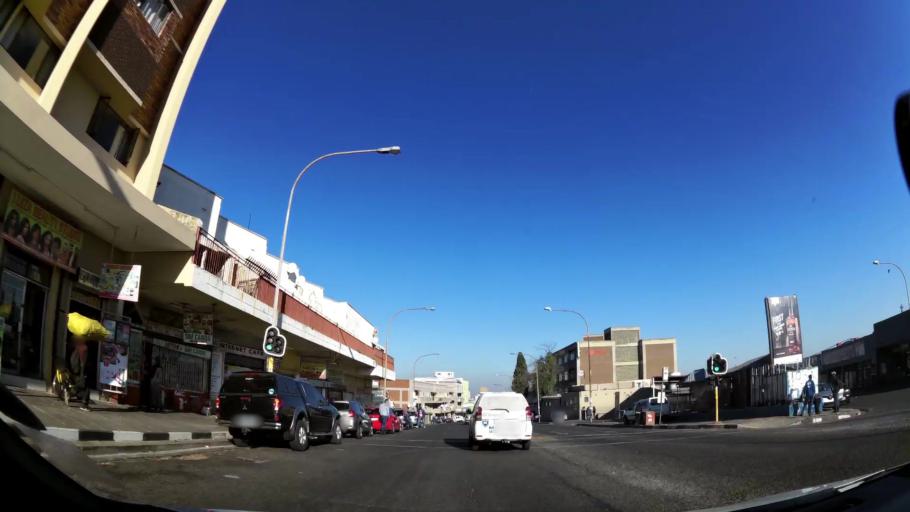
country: ZA
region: Gauteng
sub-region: City of Johannesburg Metropolitan Municipality
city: Johannesburg
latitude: -26.2014
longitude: 28.0744
